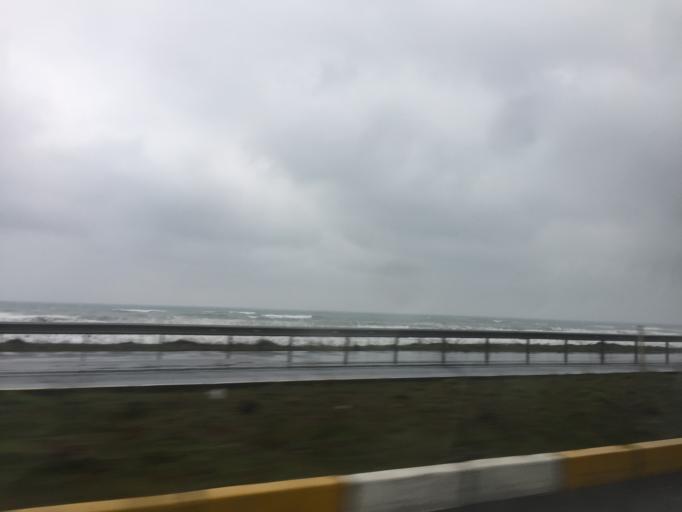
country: TR
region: Zonguldak
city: Alapli
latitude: 41.1082
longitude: 31.2670
